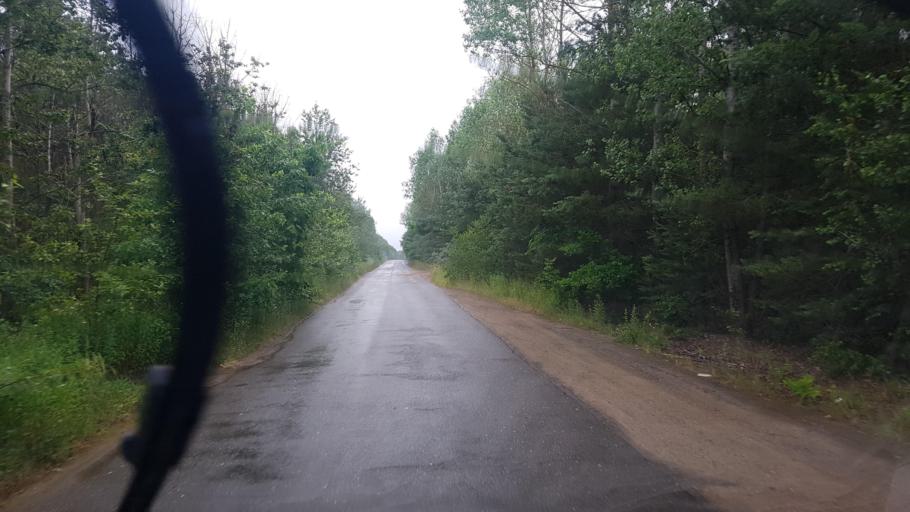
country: DE
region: Brandenburg
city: Lauchhammer
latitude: 51.5396
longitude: 13.7564
